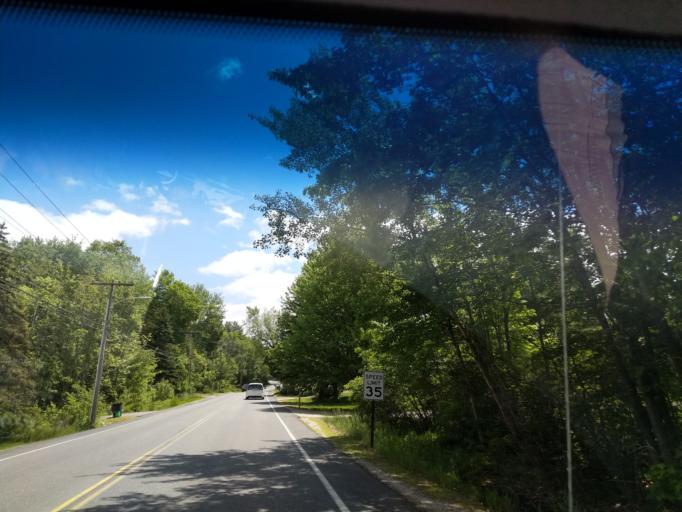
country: US
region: Maine
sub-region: Cumberland County
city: Falmouth
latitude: 43.7292
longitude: -70.2763
